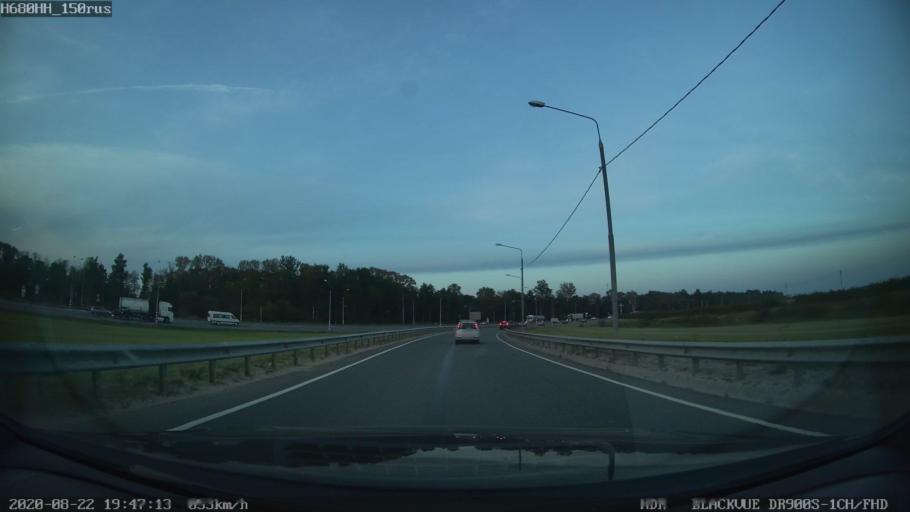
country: RU
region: Tverskaya
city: Emmaus
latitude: 56.7824
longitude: 36.0919
